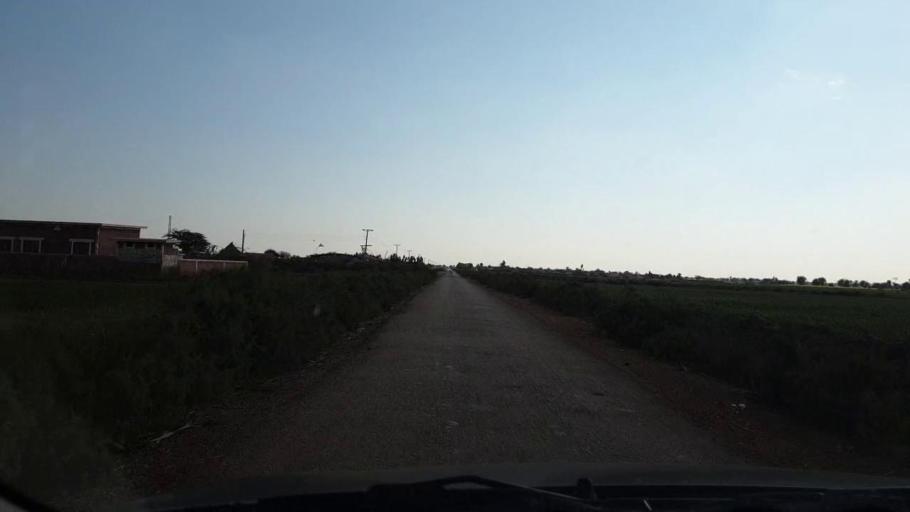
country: PK
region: Sindh
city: Sinjhoro
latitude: 25.9985
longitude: 68.8394
